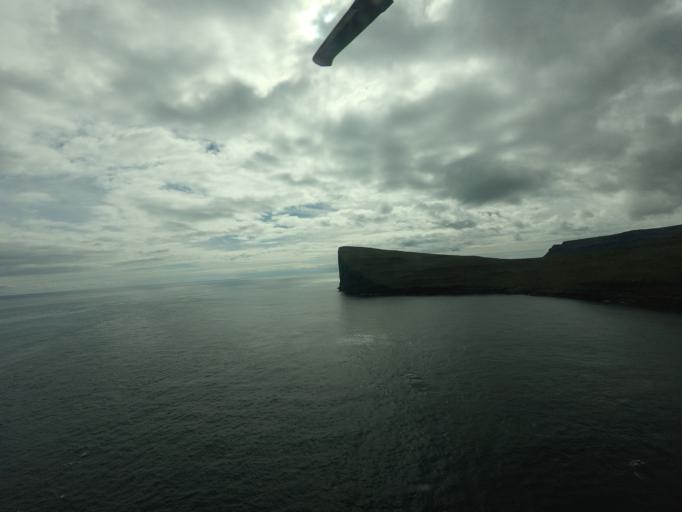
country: FO
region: Nordoyar
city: Klaksvik
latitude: 62.3091
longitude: -6.3121
